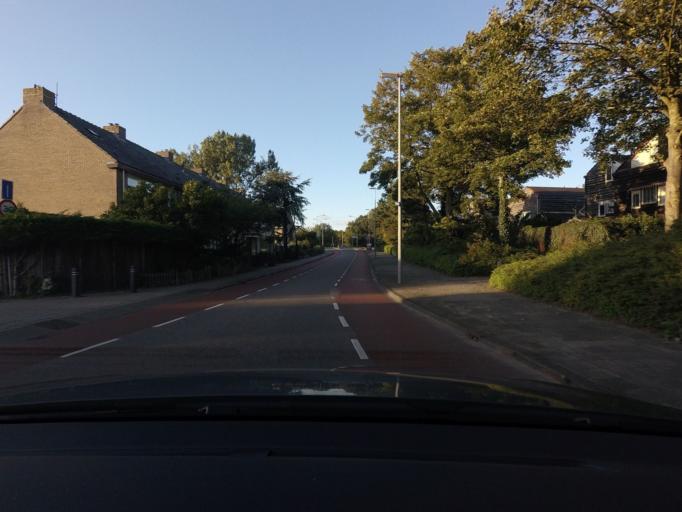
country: NL
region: North Holland
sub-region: Gemeente Alkmaar
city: Alkmaar
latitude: 52.6385
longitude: 4.7756
